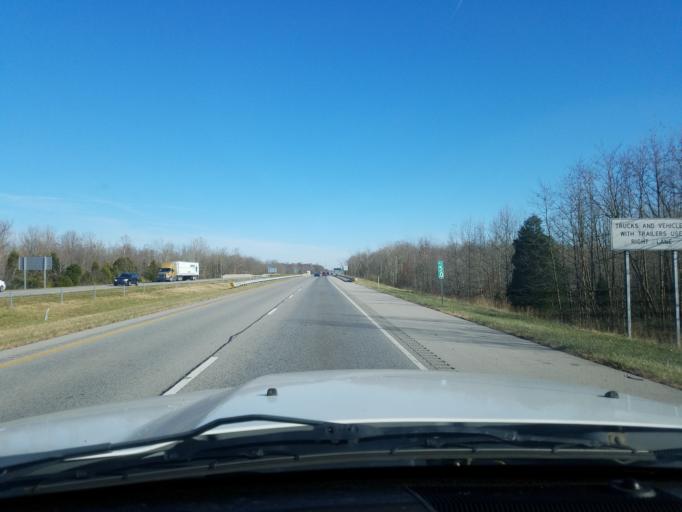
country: US
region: Indiana
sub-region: Clark County
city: Clarksville
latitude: 38.3446
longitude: -85.7865
